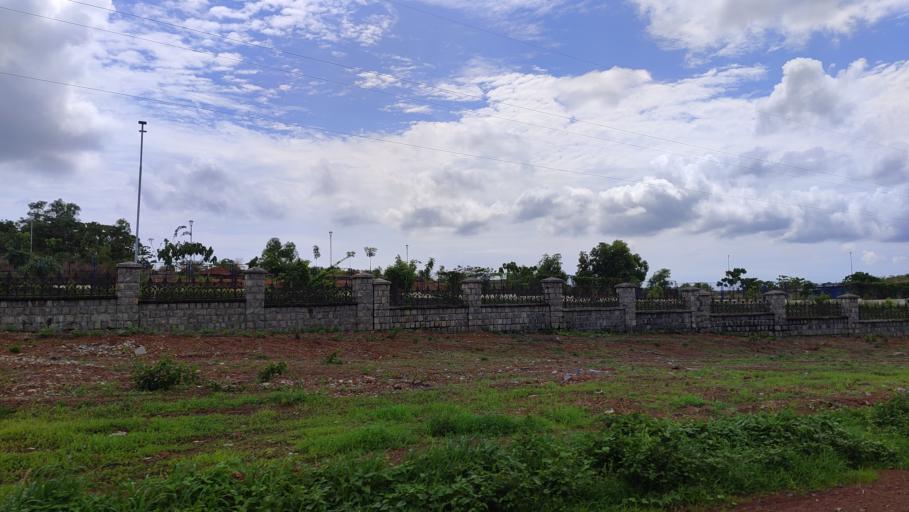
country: IN
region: Kerala
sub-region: Kasaragod District
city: Kannangad
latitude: 12.3954
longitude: 75.0966
